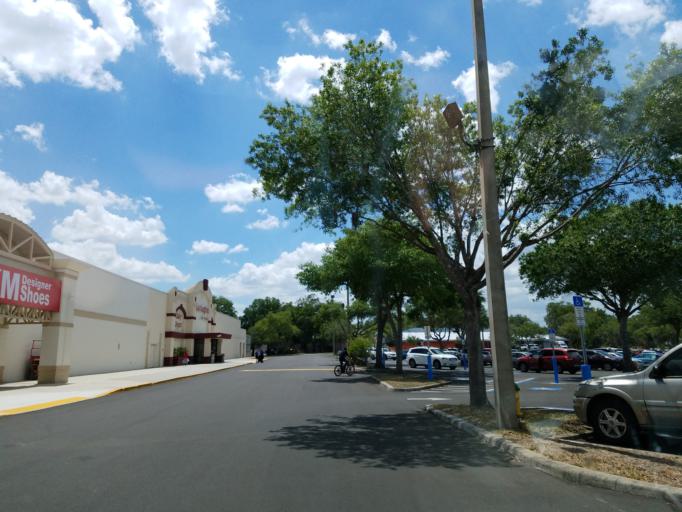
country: US
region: Florida
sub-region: Hillsborough County
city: Brandon
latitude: 27.9360
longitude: -82.2980
